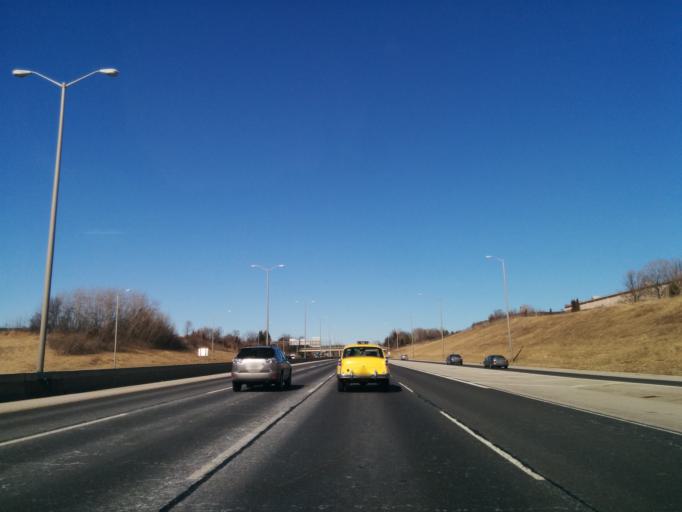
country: US
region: Illinois
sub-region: DuPage County
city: Woodridge
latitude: 41.7540
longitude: -88.0353
